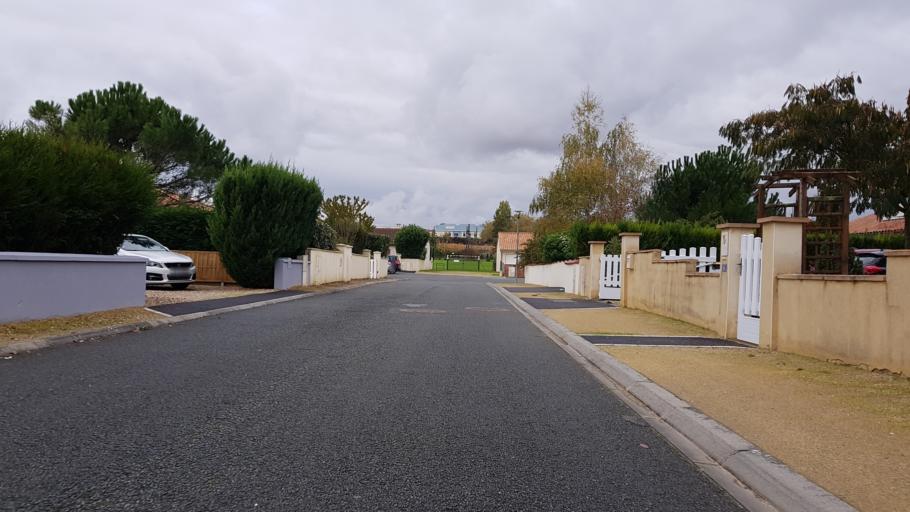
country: FR
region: Poitou-Charentes
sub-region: Departement de la Vienne
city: Chasseneuil-du-Poitou
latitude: 46.6592
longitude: 0.3800
